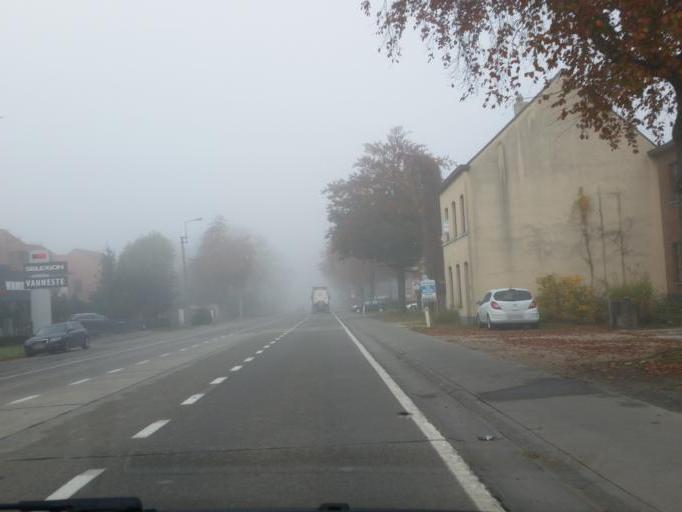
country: BE
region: Flanders
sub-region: Provincie Oost-Vlaanderen
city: Melle
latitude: 51.0214
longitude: 3.7771
